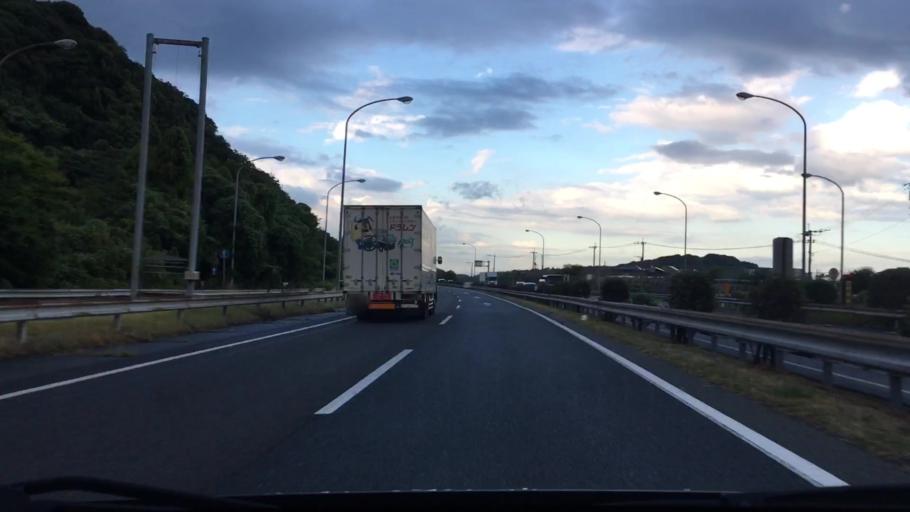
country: JP
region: Yamaguchi
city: Shimonoseki
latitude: 33.8732
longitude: 130.9659
